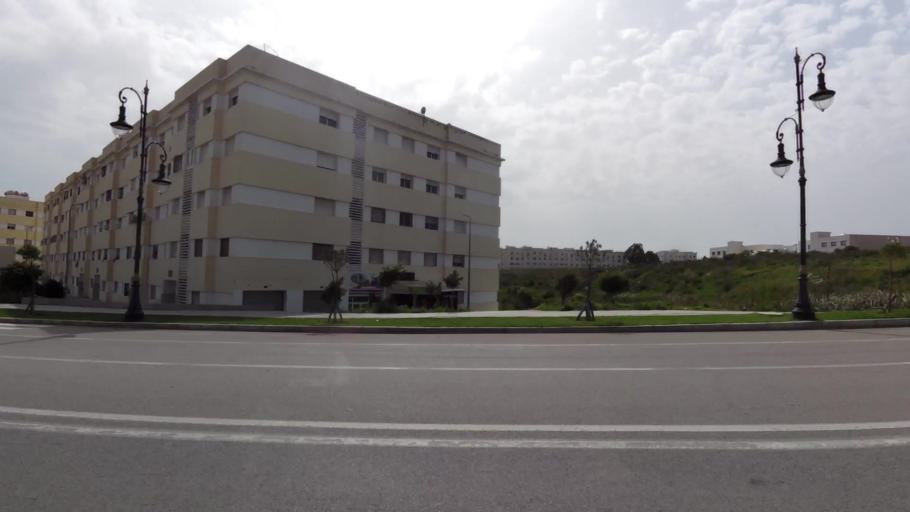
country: MA
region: Tanger-Tetouan
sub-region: Tanger-Assilah
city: Boukhalef
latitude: 35.7371
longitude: -5.8744
